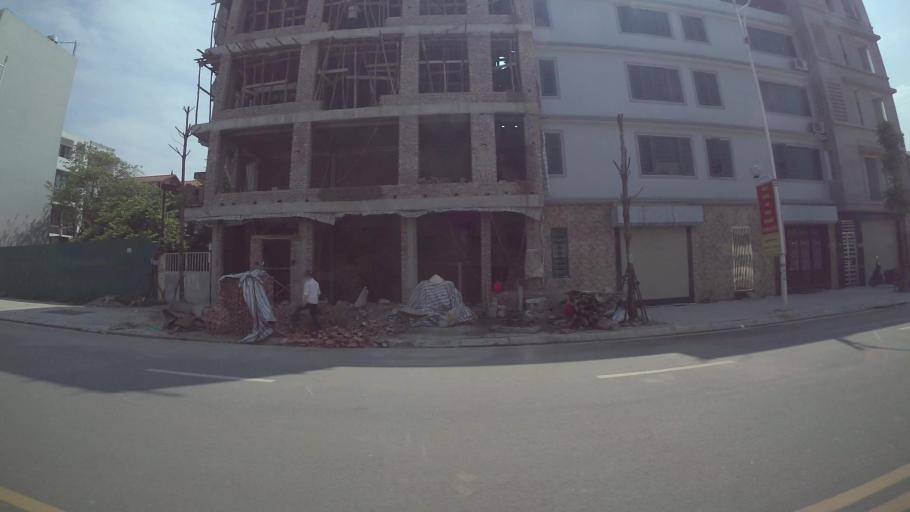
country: VN
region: Ha Noi
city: Hoan Kiem
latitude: 21.0628
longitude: 105.8678
